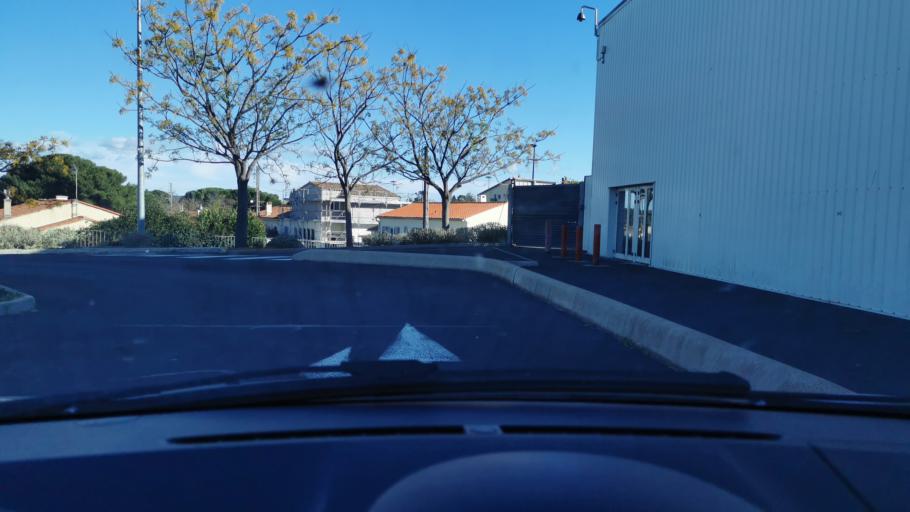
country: FR
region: Languedoc-Roussillon
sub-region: Departement de l'Herault
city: Sete
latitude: 43.4095
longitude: 3.6694
